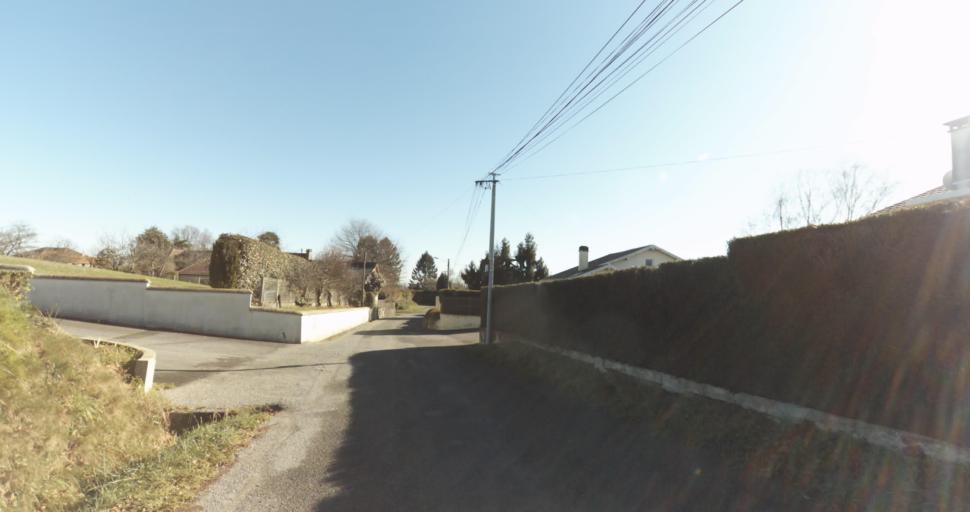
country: FR
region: Aquitaine
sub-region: Departement des Pyrenees-Atlantiques
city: Morlaas
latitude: 43.3385
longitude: -0.2731
